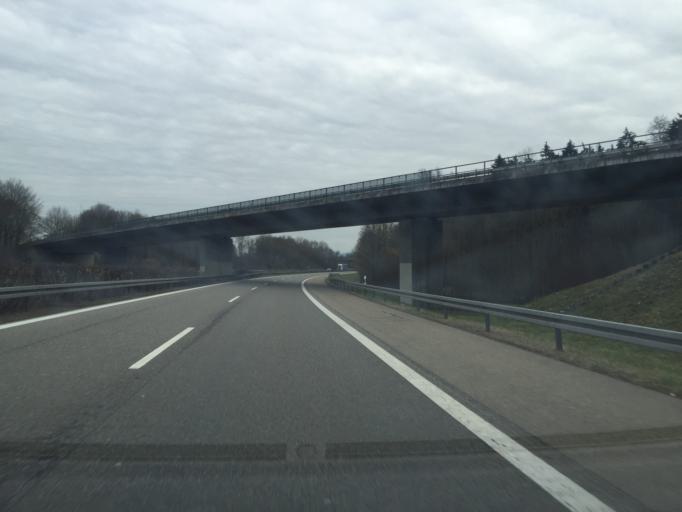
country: DE
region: Baden-Wuerttemberg
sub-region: Freiburg Region
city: Volkertshausen
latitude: 47.8098
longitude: 8.8544
